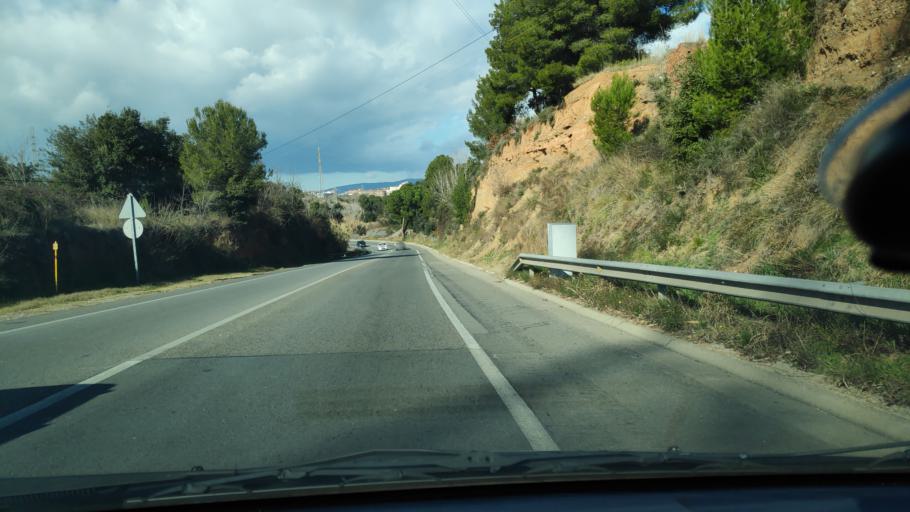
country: ES
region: Catalonia
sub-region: Provincia de Barcelona
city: Terrassa
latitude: 41.5547
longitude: 2.0520
